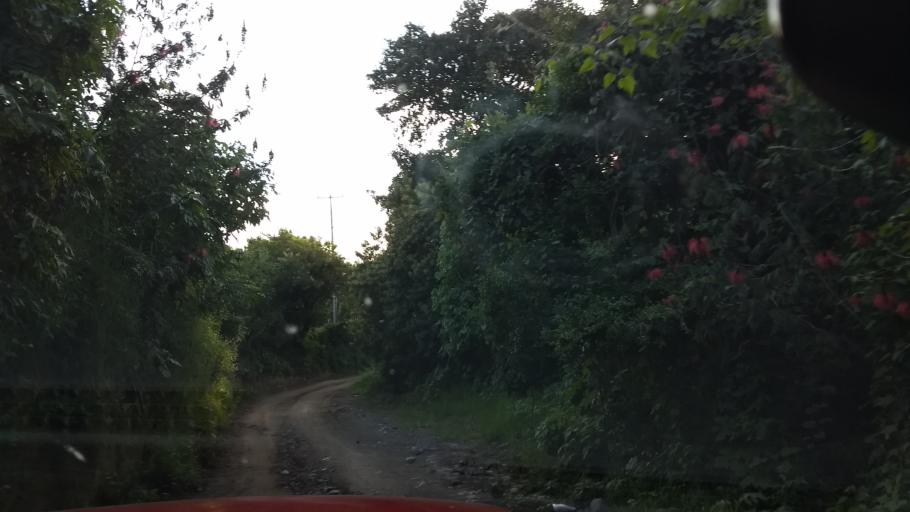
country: MX
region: Jalisco
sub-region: San Gabriel
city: Alista
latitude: 19.5048
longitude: -103.7592
